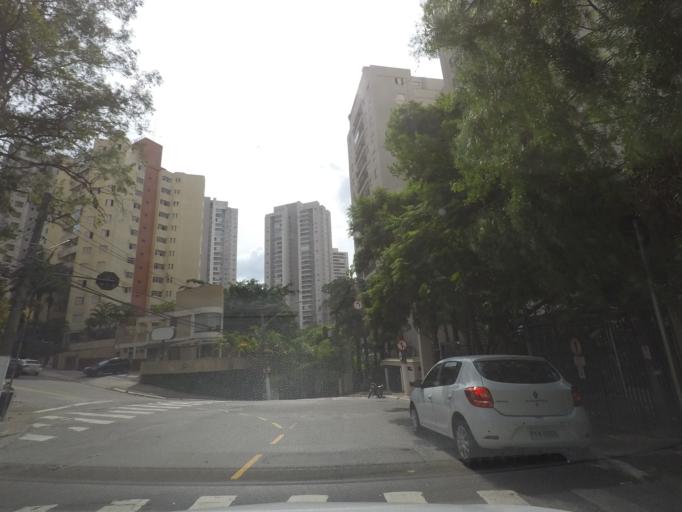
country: BR
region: Sao Paulo
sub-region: Taboao Da Serra
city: Taboao da Serra
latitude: -23.6326
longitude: -46.7382
